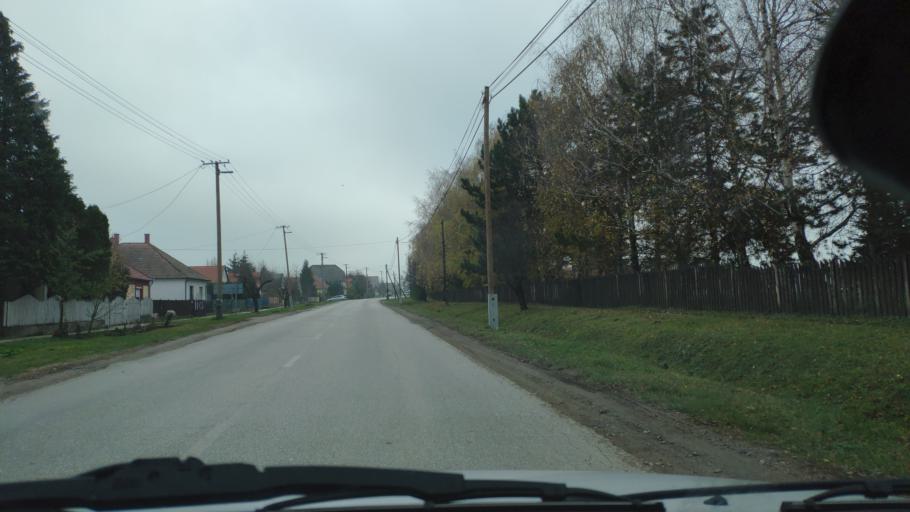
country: HU
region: Somogy
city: Balatonbereny
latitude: 46.6725
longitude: 17.2901
